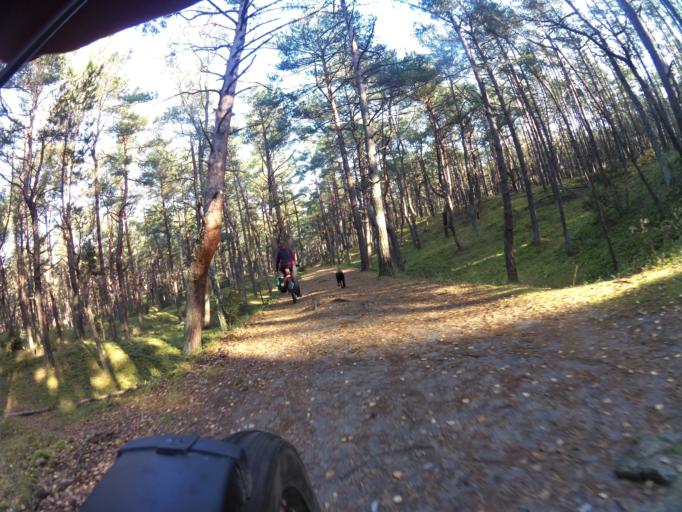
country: PL
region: Pomeranian Voivodeship
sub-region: Powiat pucki
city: Hel
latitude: 54.5971
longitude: 18.8126
